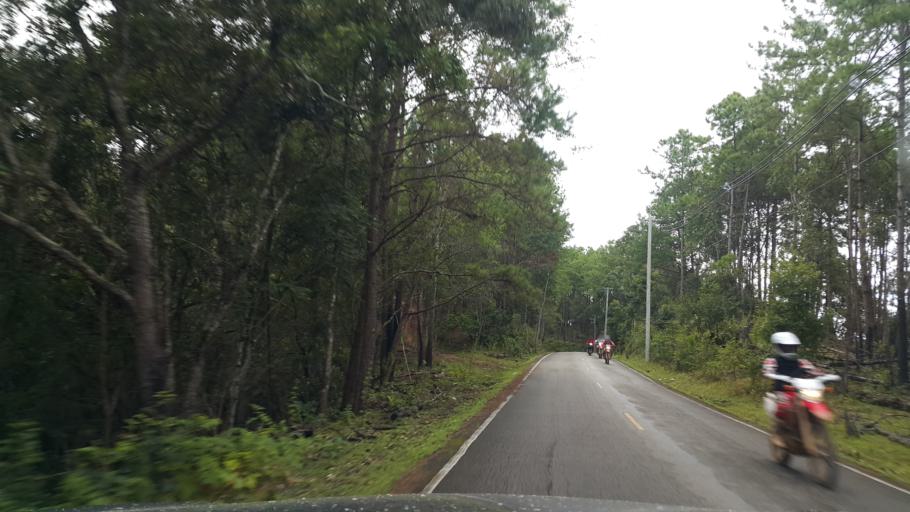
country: TH
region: Chiang Mai
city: Samoeng
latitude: 18.9112
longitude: 98.5029
